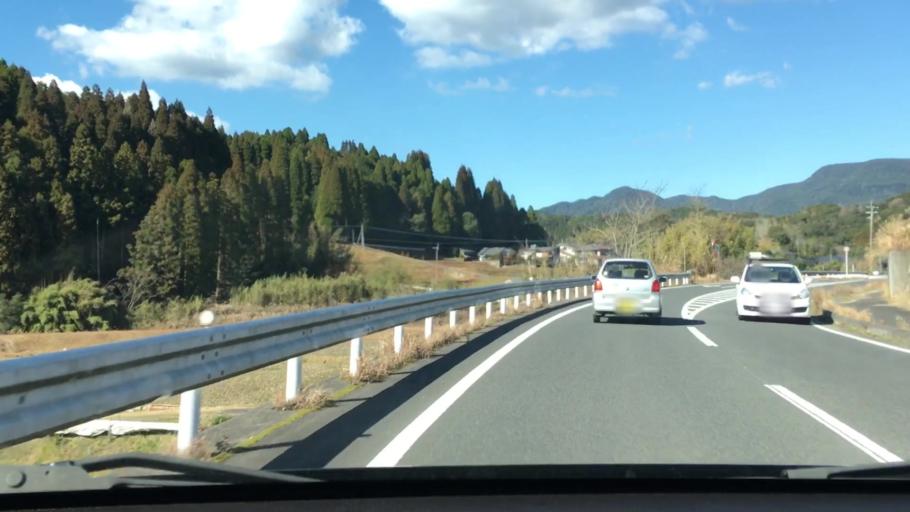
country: JP
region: Kagoshima
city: Ijuin
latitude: 31.6936
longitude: 130.4621
